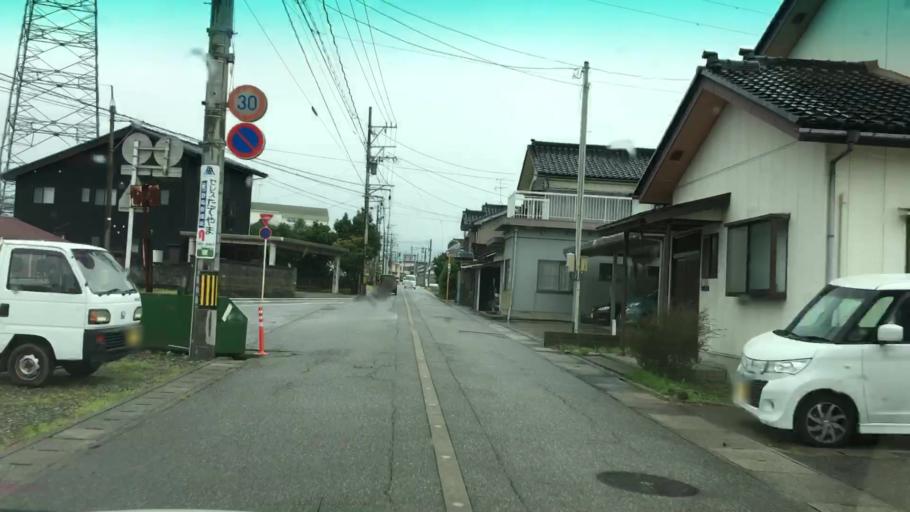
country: JP
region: Toyama
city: Kamiichi
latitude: 36.6523
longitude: 137.3192
